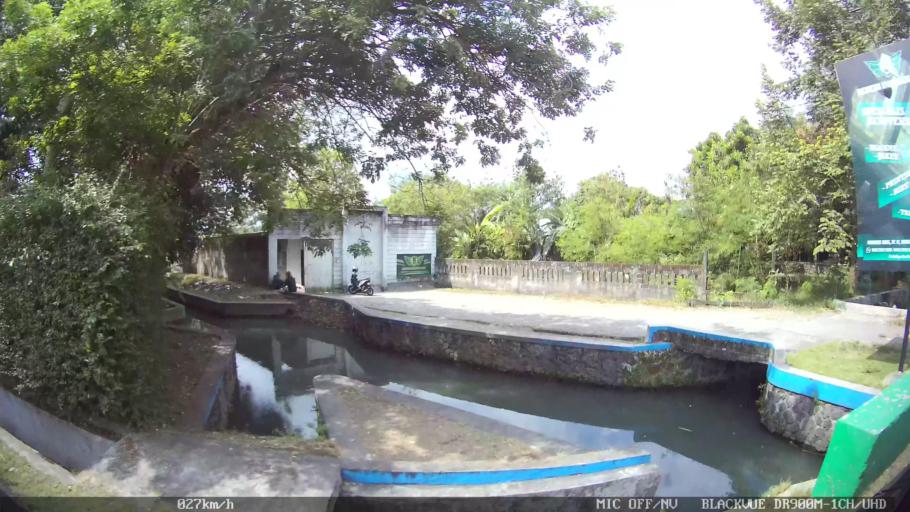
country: ID
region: Daerah Istimewa Yogyakarta
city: Kasihan
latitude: -7.8107
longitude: 110.3353
